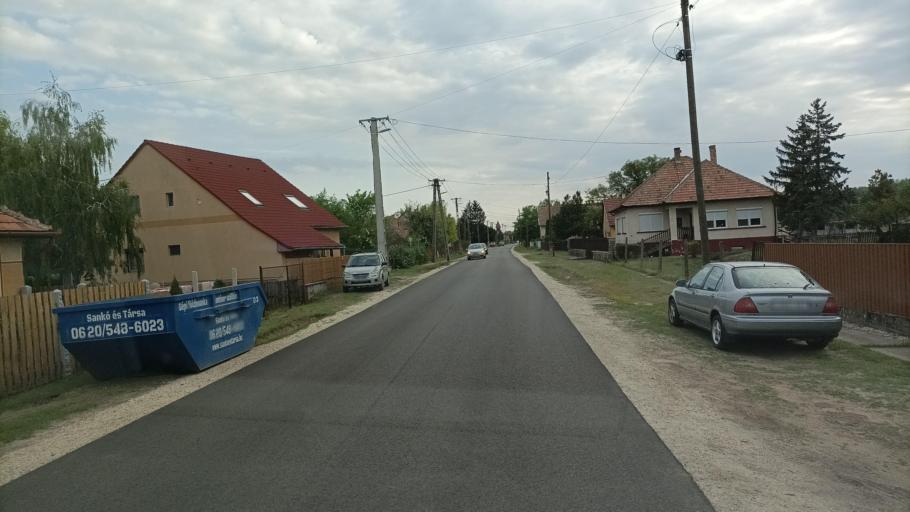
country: HU
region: Pest
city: Monor
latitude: 47.2903
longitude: 19.4217
